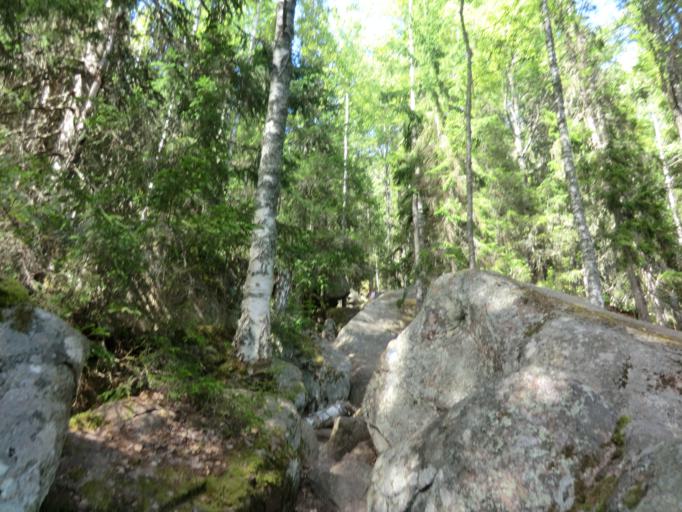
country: SE
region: Vaesternorrland
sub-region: Kramfors Kommun
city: Nordingra
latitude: 63.0727
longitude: 18.3518
